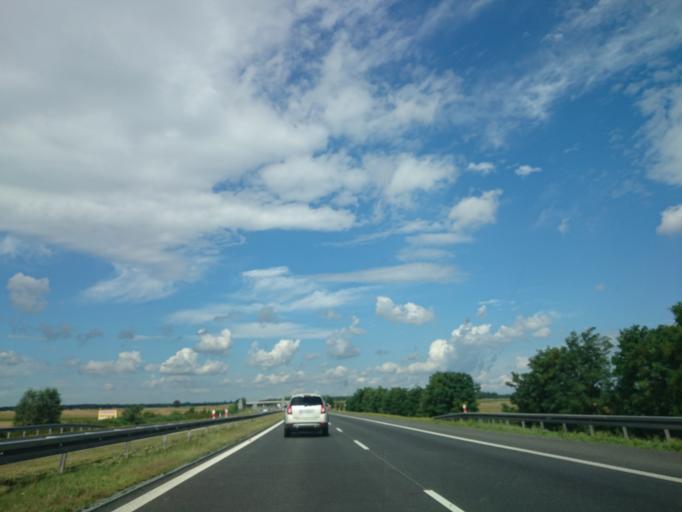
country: PL
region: Opole Voivodeship
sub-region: Powiat opolski
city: Proszkow
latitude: 50.5732
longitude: 17.8535
